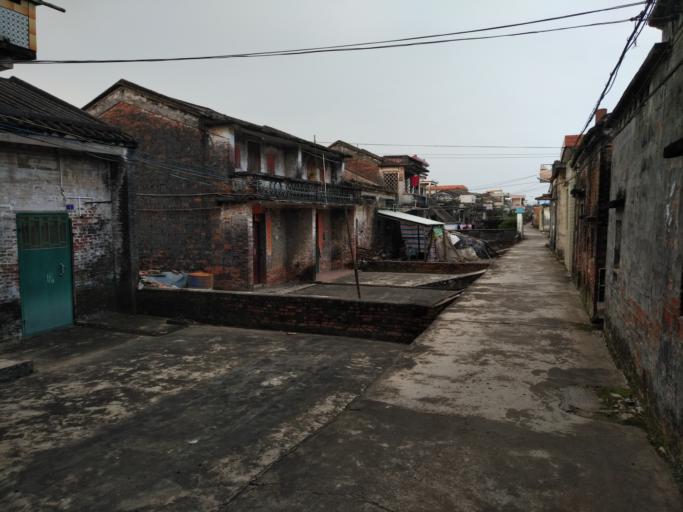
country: CN
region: Guangdong
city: Da'ao
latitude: 22.4555
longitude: 113.2113
